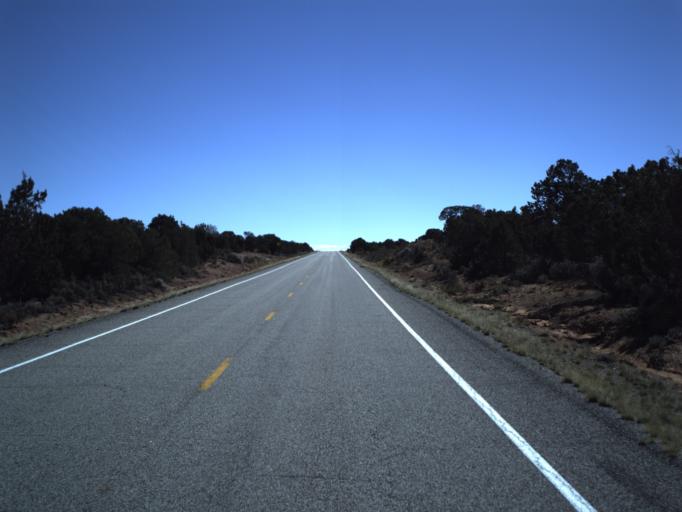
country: US
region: Utah
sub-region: San Juan County
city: Blanding
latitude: 37.5508
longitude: -109.9916
